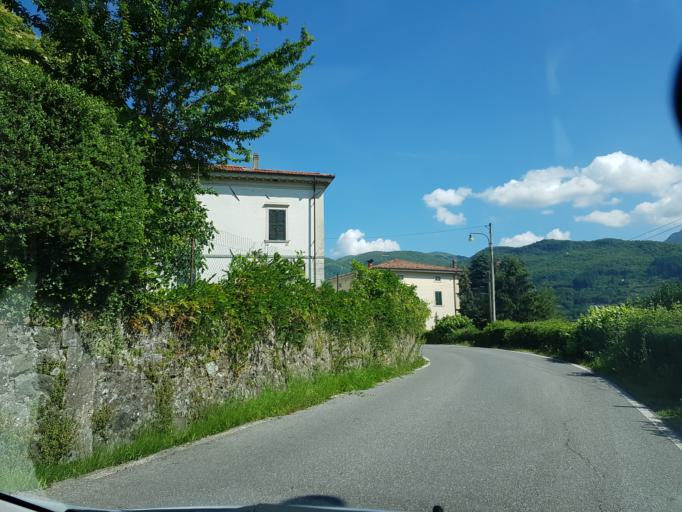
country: IT
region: Tuscany
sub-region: Provincia di Lucca
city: Camporgiano
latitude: 44.1562
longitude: 10.3359
